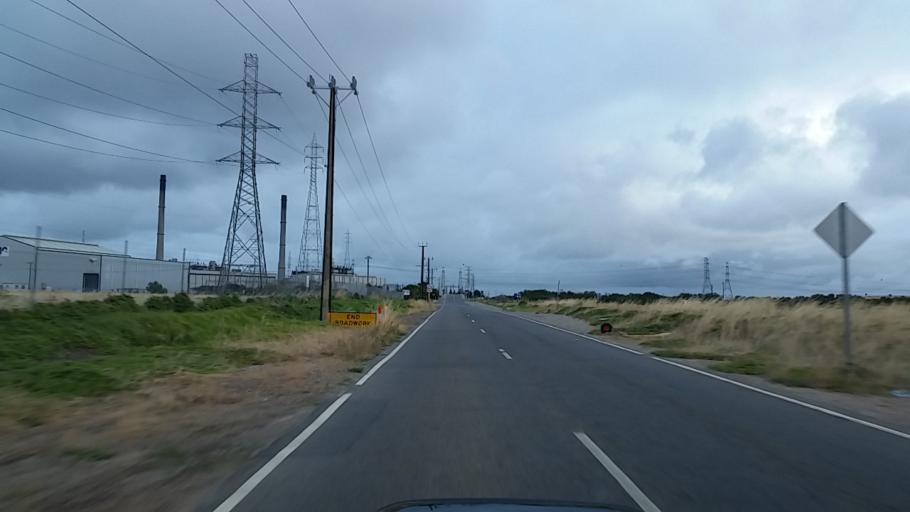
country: AU
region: South Australia
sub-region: Port Adelaide Enfield
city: Birkenhead
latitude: -34.8158
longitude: 138.5252
